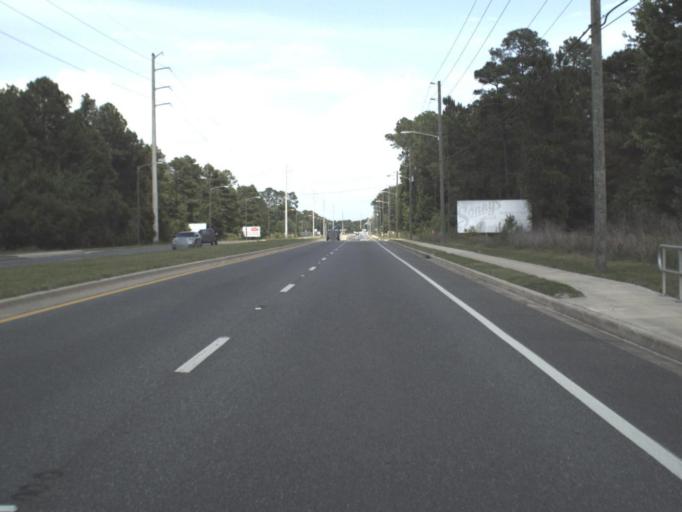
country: US
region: Florida
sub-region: Putnam County
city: Palatka
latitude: 29.6373
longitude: -81.7006
